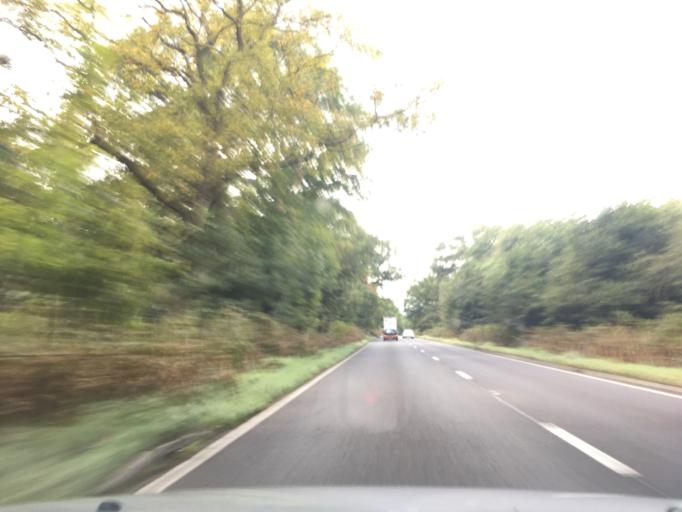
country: GB
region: England
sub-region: Hampshire
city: Liphook
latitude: 51.0892
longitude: -0.7803
